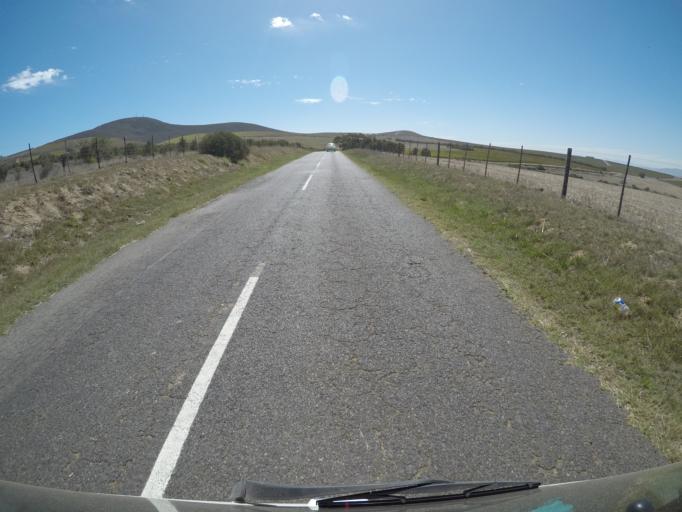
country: ZA
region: Western Cape
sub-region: City of Cape Town
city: Sunset Beach
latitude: -33.7250
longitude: 18.5702
